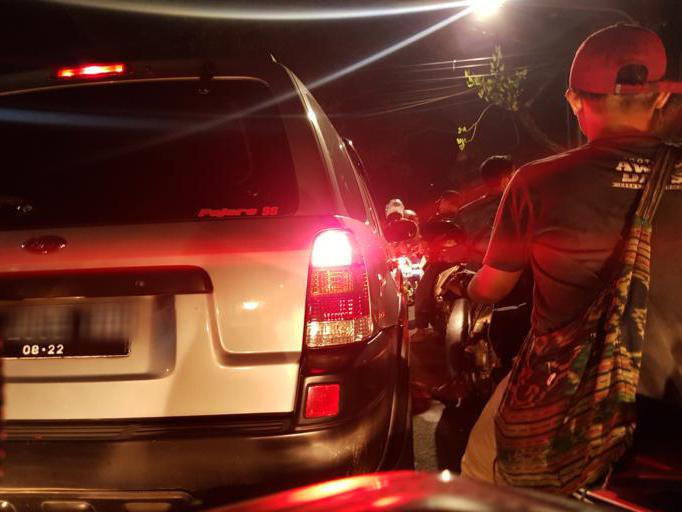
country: ID
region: West Java
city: Cileungsir
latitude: -6.3141
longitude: 106.9119
